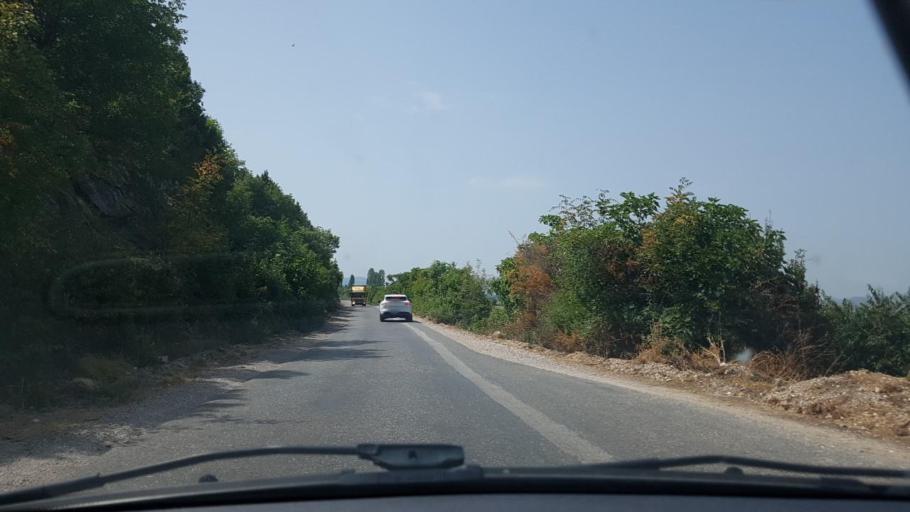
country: BA
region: Federation of Bosnia and Herzegovina
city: Tasovcici
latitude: 43.0323
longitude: 17.7387
